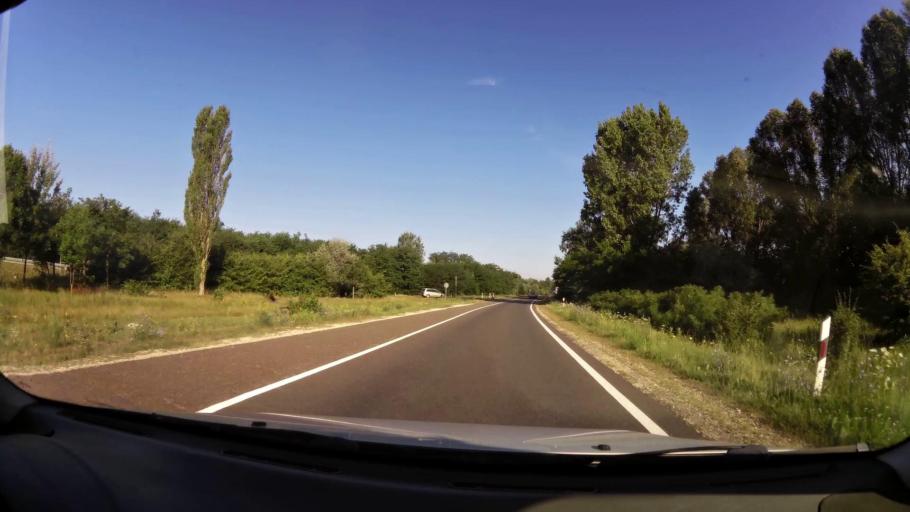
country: HU
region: Pest
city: Albertirsa
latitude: 47.2624
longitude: 19.5839
